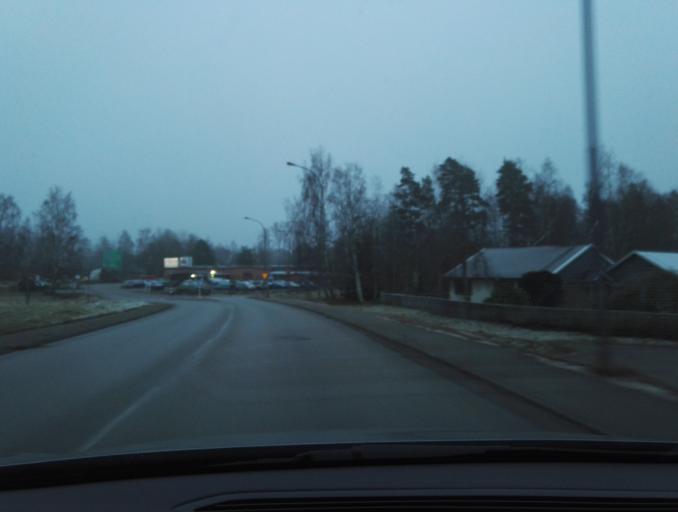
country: SE
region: Kronoberg
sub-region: Vaxjo Kommun
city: Vaexjoe
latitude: 56.8944
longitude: 14.7366
